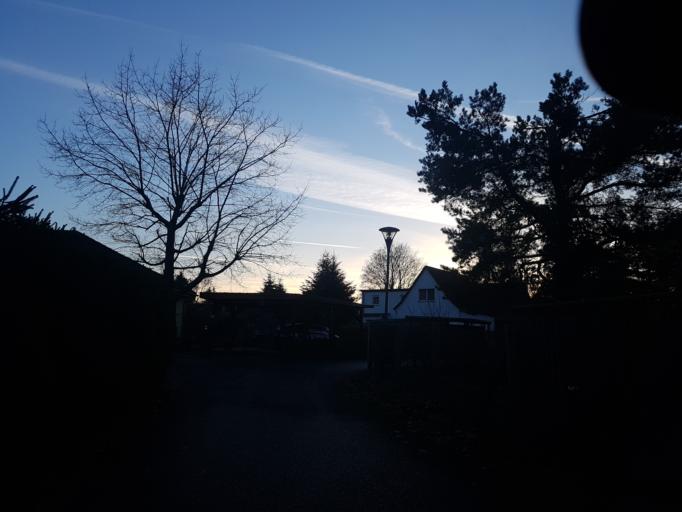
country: DE
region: Brandenburg
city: Finsterwalde
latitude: 51.6461
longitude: 13.6918
